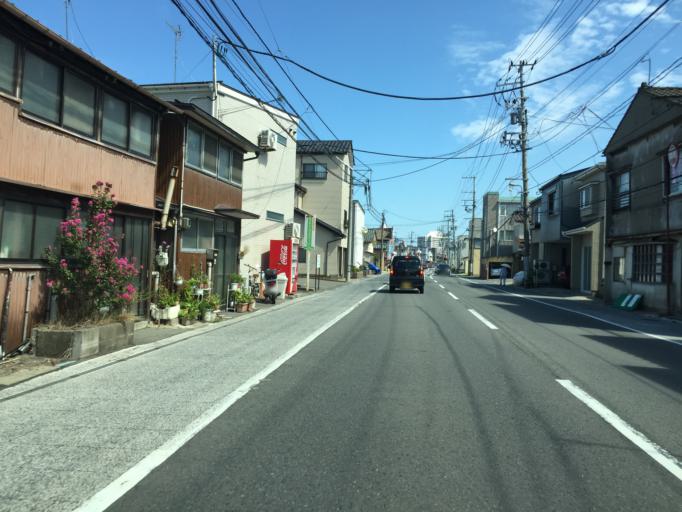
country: JP
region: Niigata
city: Niigata-shi
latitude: 37.9122
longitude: 139.0286
